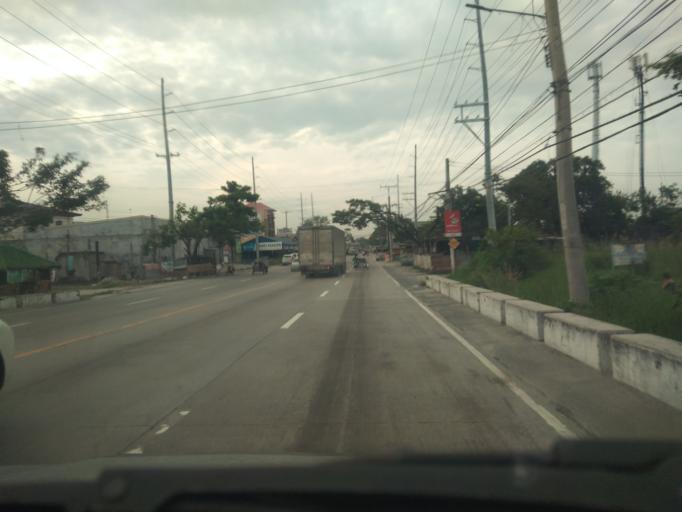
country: PH
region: Central Luzon
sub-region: Province of Pampanga
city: San Fernando
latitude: 15.0265
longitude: 120.6974
